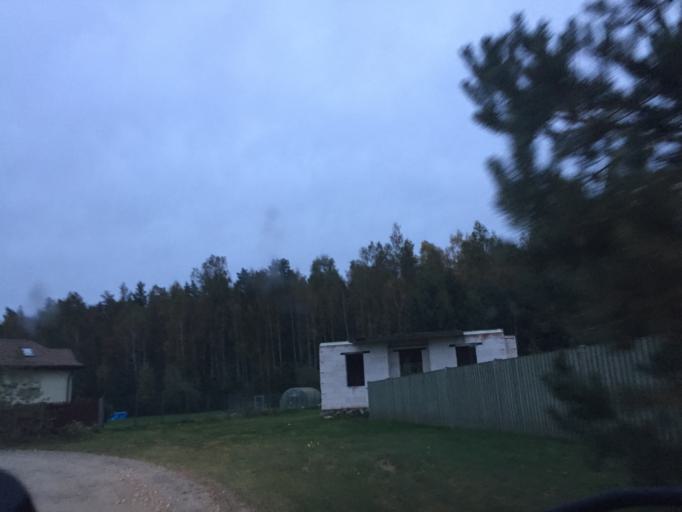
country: LV
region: Adazi
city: Adazi
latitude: 57.0871
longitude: 24.3754
